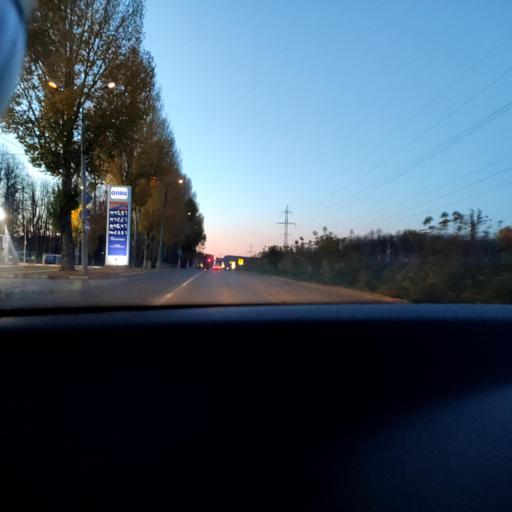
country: RU
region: Samara
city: Petra-Dubrava
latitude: 53.3057
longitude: 50.2800
